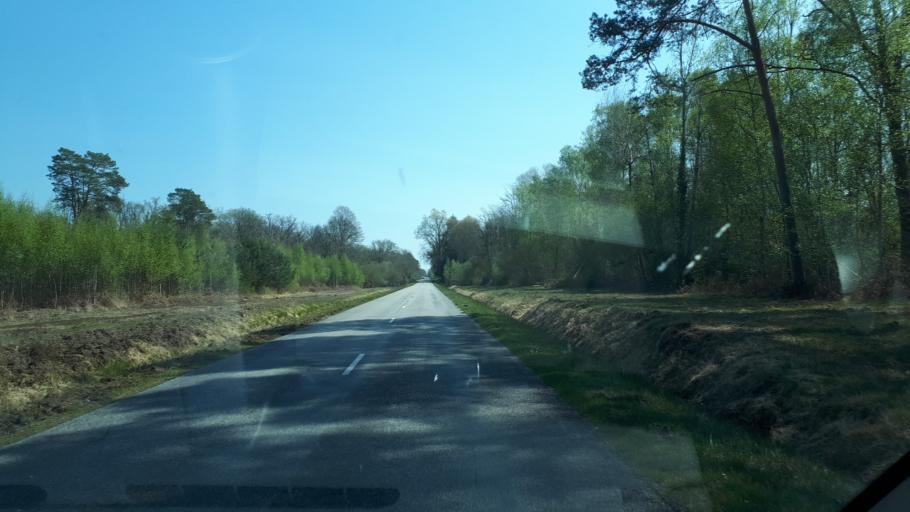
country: FR
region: Centre
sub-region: Departement du Loir-et-Cher
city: Theillay
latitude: 47.3161
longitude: 2.1247
